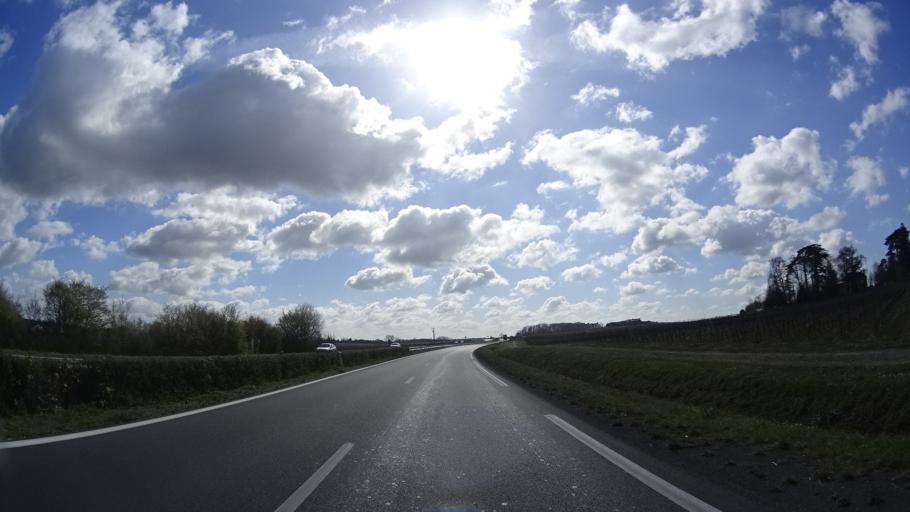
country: FR
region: Pays de la Loire
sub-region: Departement de Maine-et-Loire
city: Juigne-sur-Loire
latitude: 47.3805
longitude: -0.4753
